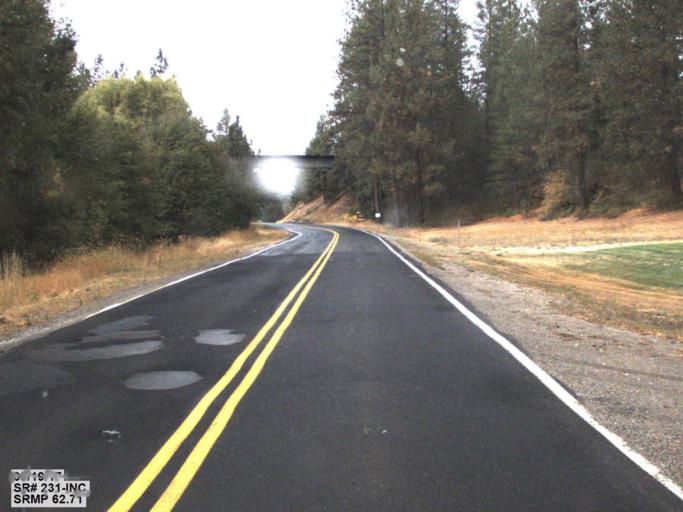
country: US
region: Washington
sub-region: Stevens County
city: Chewelah
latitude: 48.0572
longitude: -117.7503
